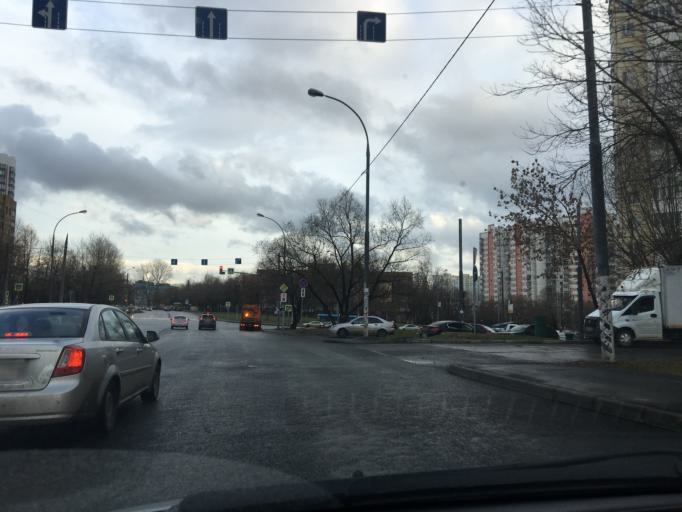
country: RU
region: Moscow
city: Tsaritsyno
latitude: 55.6442
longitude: 37.6543
